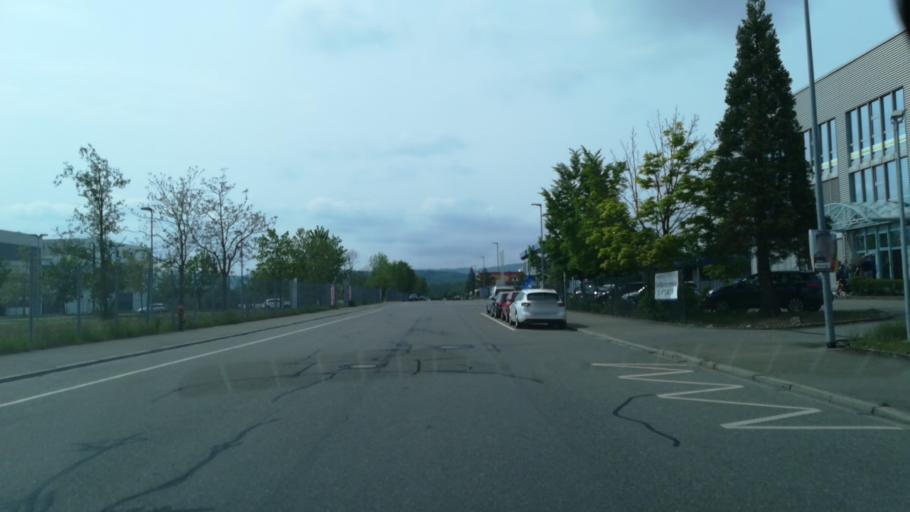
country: DE
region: Baden-Wuerttemberg
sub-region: Freiburg Region
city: Singen
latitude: 47.7566
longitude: 8.8729
